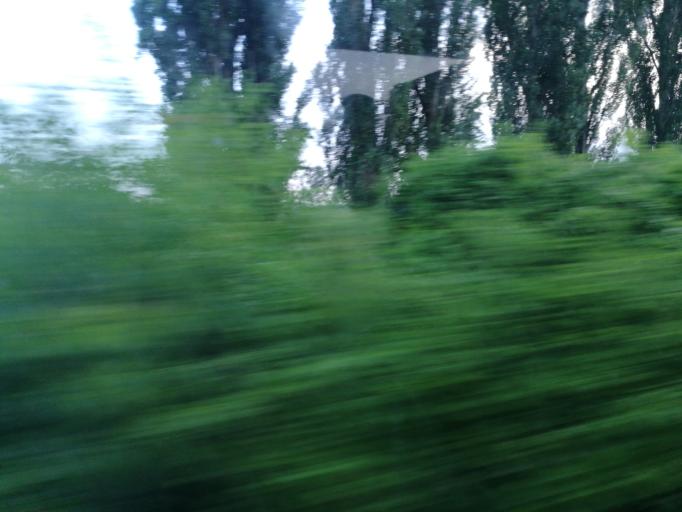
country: RO
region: Dambovita
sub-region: Comuna Contesti
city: Contesti
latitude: 44.6561
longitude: 25.6571
